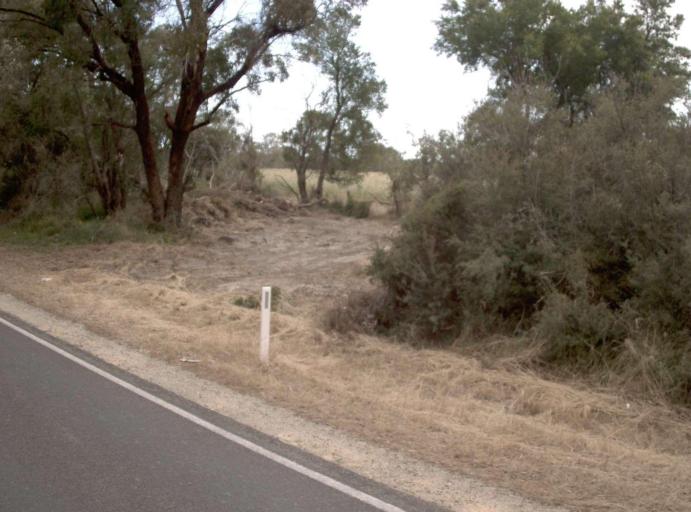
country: AU
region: Victoria
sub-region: Wellington
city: Sale
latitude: -38.2072
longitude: 147.1000
